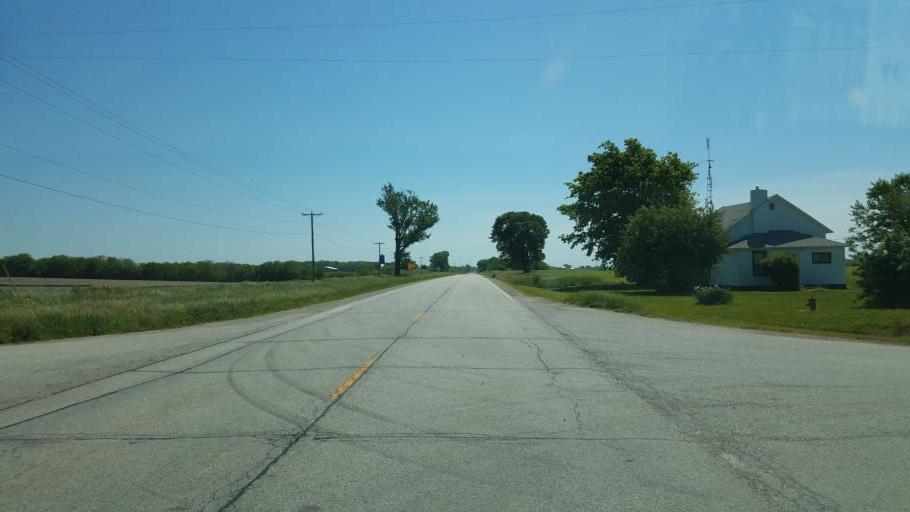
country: US
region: Illinois
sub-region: McLean County
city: Heyworth
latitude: 40.3121
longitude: -89.0360
